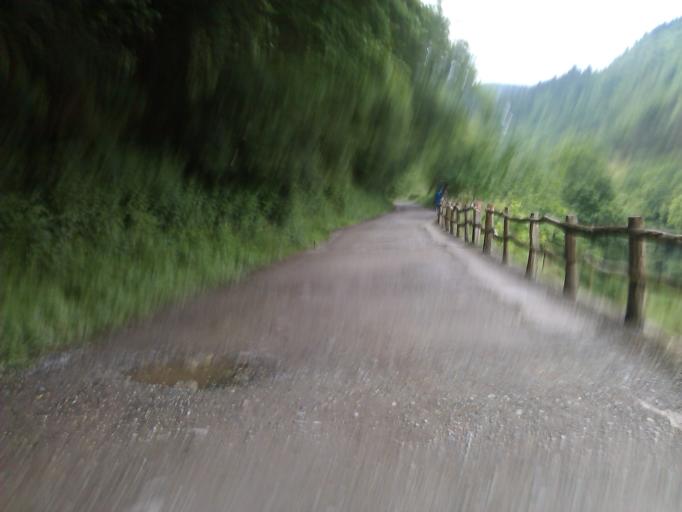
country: ES
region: Basque Country
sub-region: Provincia de Guipuzcoa
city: Andoain
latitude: 43.1977
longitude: -2.0106
